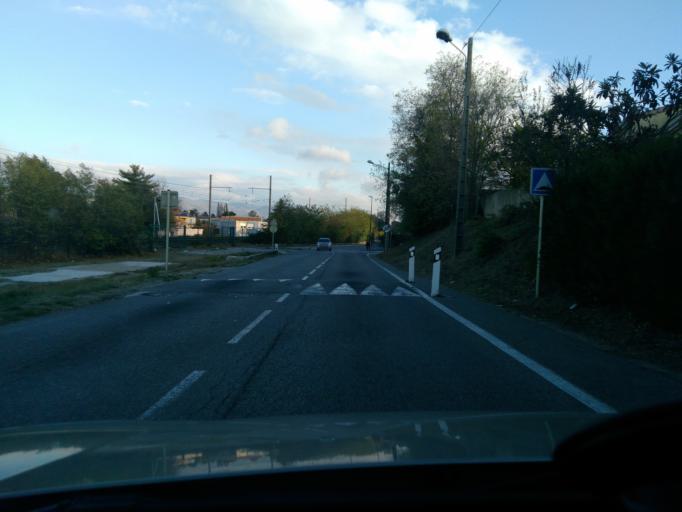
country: FR
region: Rhone-Alpes
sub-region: Departement de la Drome
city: Montelimar
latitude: 44.5457
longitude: 4.7407
